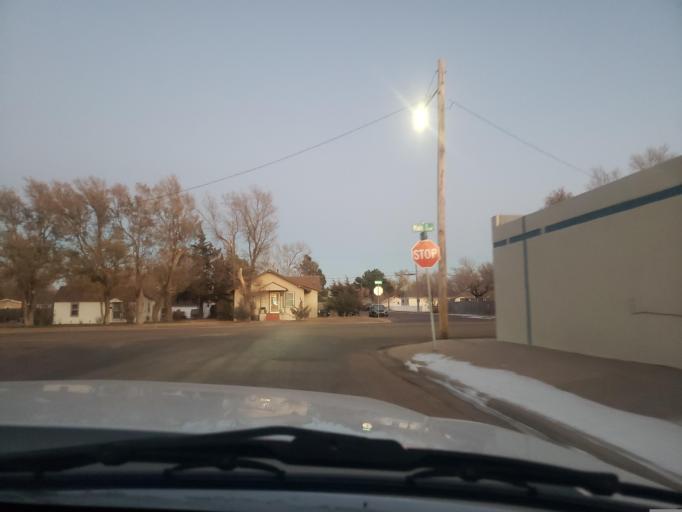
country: US
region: Kansas
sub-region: Finney County
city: Garden City
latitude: 37.9841
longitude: -100.8697
